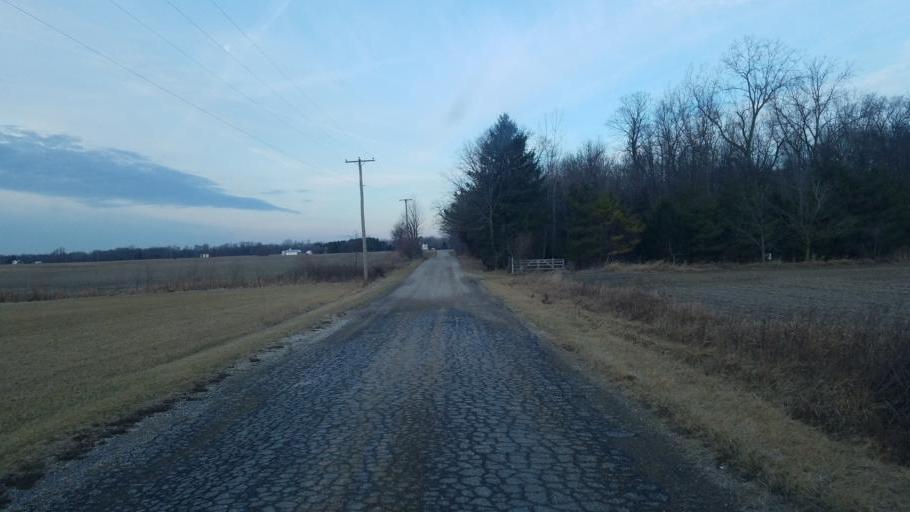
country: US
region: Ohio
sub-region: Morrow County
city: Cardington
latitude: 40.5091
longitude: -82.8593
